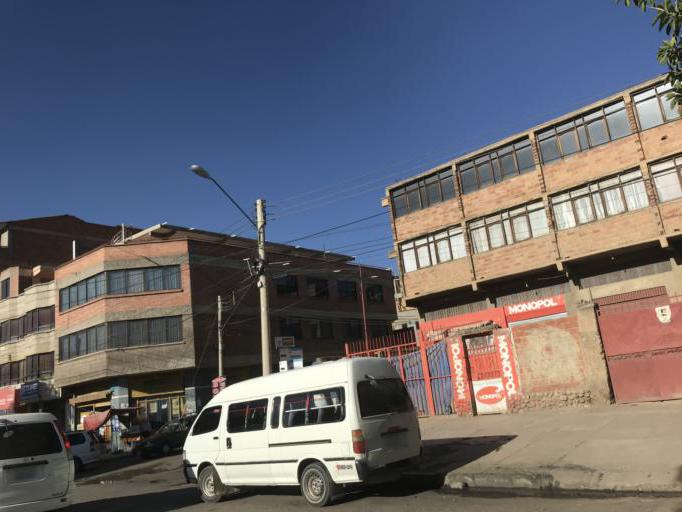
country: BO
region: Cochabamba
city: Cochabamba
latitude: -17.4186
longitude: -66.1519
